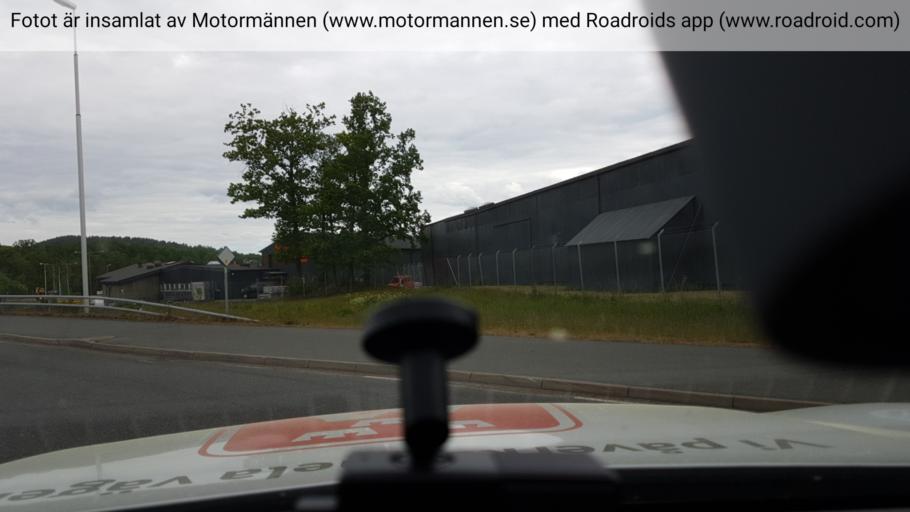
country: SE
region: Joenkoeping
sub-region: Jonkopings Kommun
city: Jonkoping
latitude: 57.7566
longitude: 14.1385
